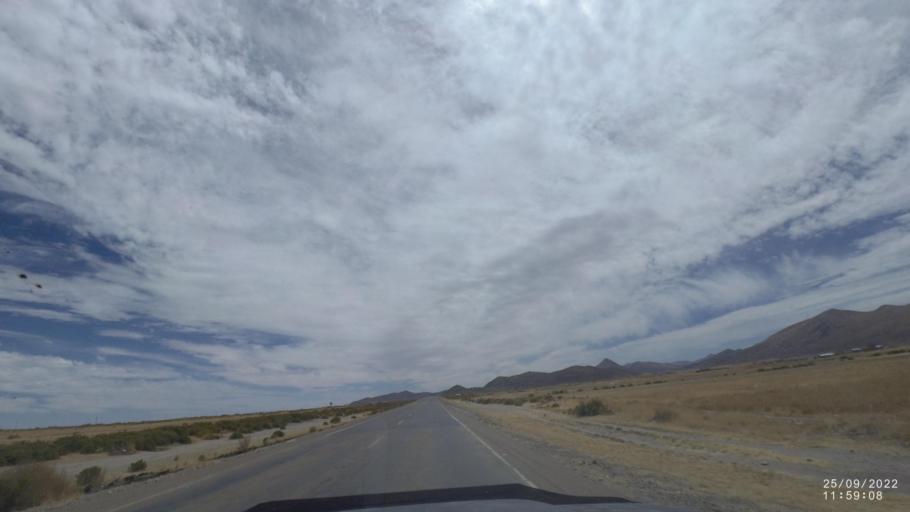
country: BO
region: Oruro
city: Challapata
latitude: -18.7926
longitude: -66.8443
